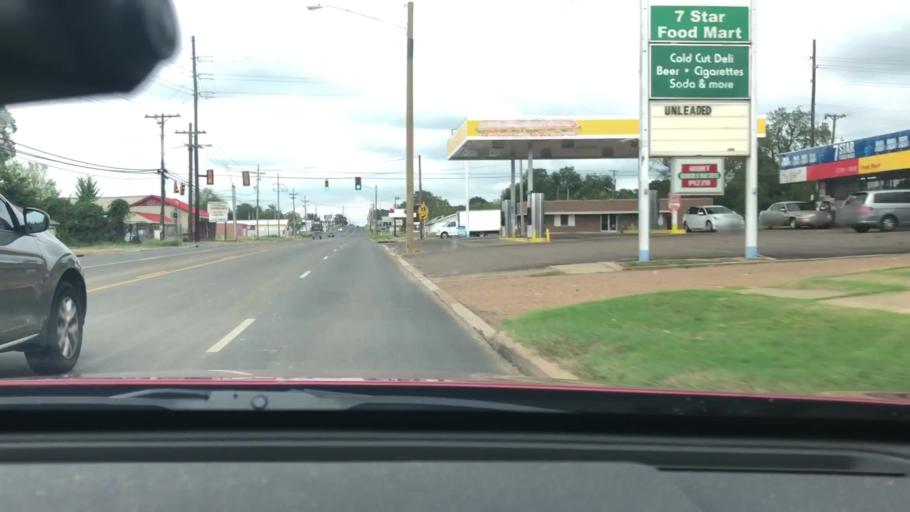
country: US
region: Arkansas
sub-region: Miller County
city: Texarkana
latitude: 33.4307
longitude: -94.0236
